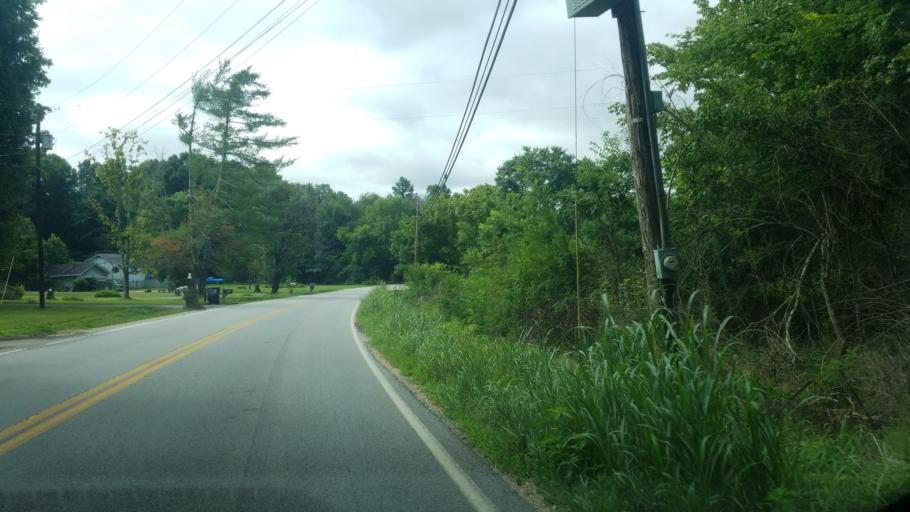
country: US
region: Tennessee
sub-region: Hamilton County
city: Lakesite
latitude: 35.1870
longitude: -85.0668
